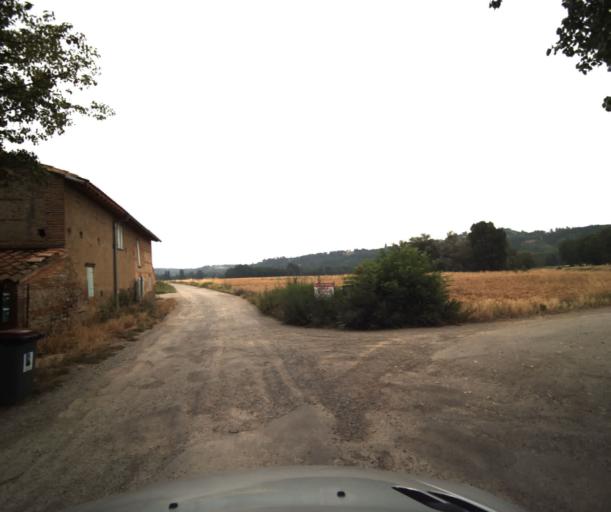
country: FR
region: Midi-Pyrenees
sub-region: Departement de la Haute-Garonne
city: Portet-sur-Garonne
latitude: 43.5314
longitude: 1.4187
